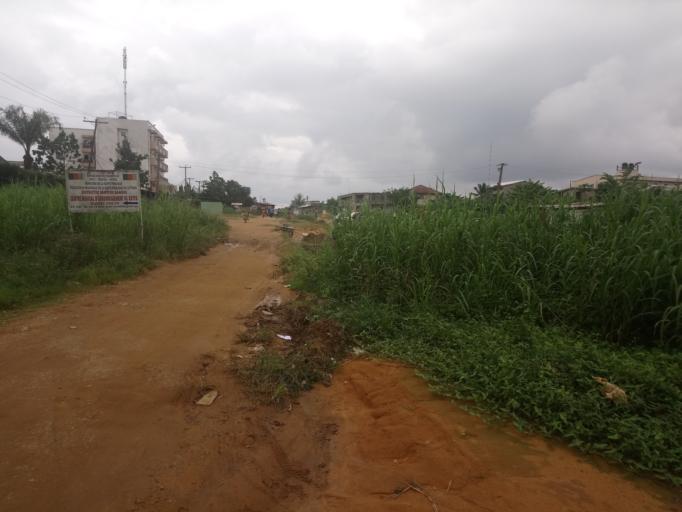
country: CM
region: Littoral
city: Douala
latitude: 4.0942
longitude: 9.7642
